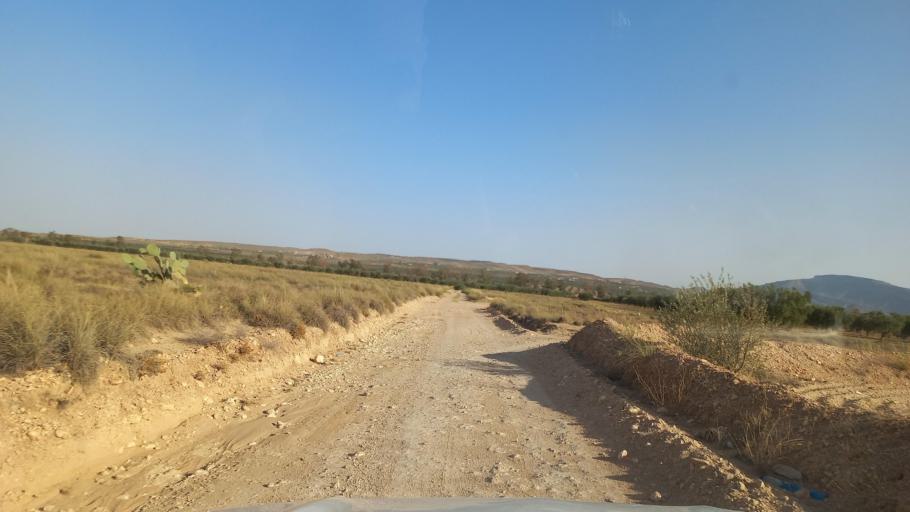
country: TN
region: Al Qasrayn
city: Kasserine
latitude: 35.2293
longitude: 8.9421
